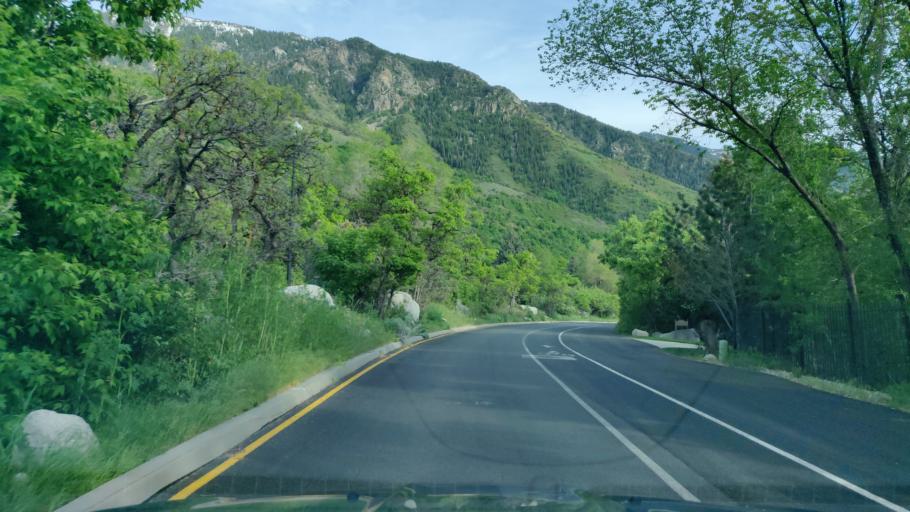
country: US
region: Utah
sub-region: Salt Lake County
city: Granite
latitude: 40.5593
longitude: -111.8003
